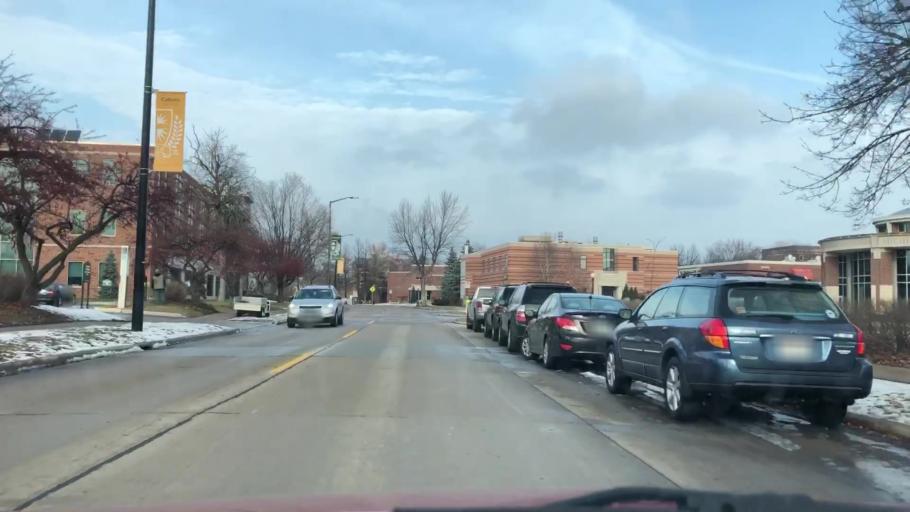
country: US
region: Wisconsin
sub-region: Brown County
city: De Pere
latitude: 44.4429
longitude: -88.0689
